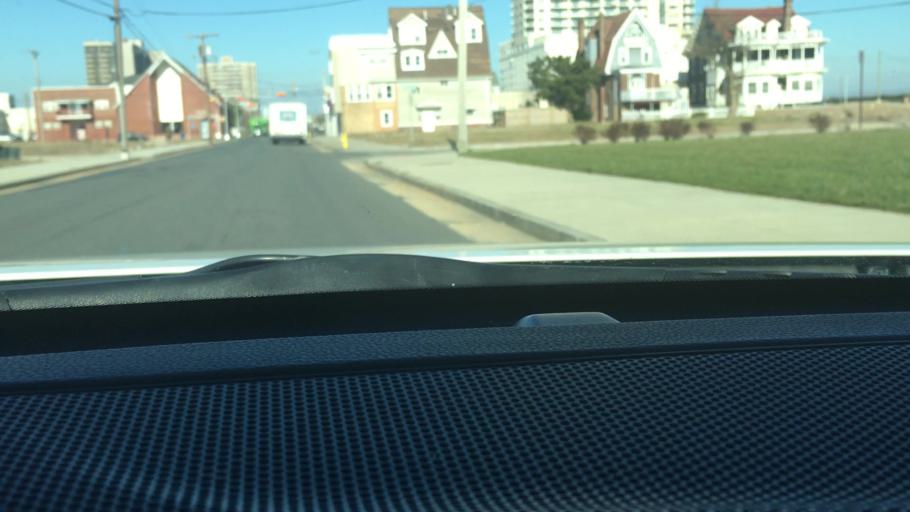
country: US
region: New Jersey
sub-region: Atlantic County
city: Atlantic City
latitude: 39.3672
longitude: -74.4123
